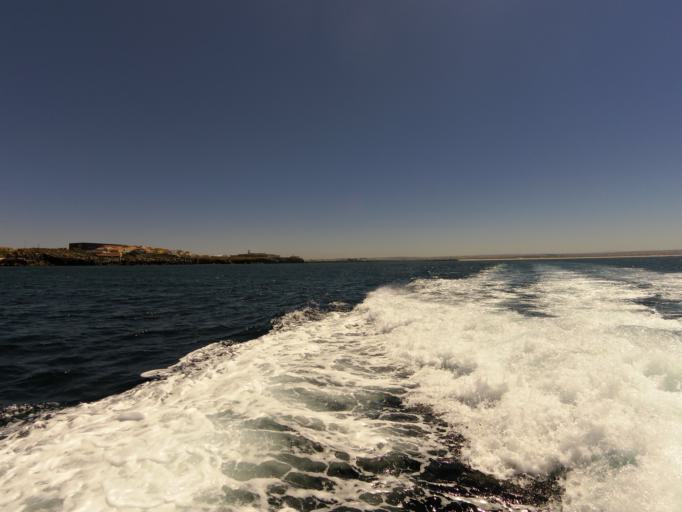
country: PT
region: Leiria
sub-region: Peniche
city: Peniche
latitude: 39.3505
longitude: -9.3911
